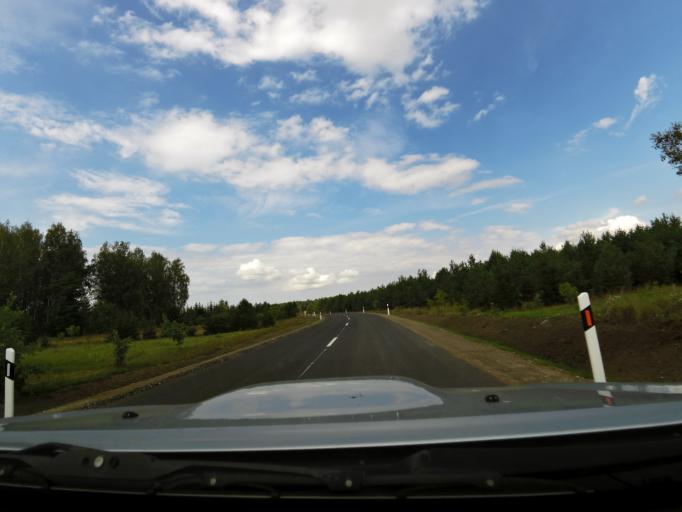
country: LT
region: Vilnius County
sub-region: Vilniaus Rajonas
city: Vievis
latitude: 54.8704
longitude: 24.8433
